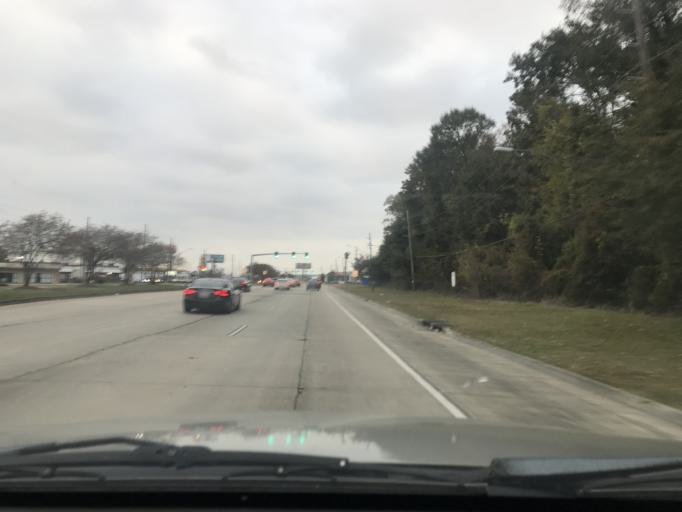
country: US
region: Louisiana
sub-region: Jefferson Parish
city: Woodmere
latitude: 29.8715
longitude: -90.0794
